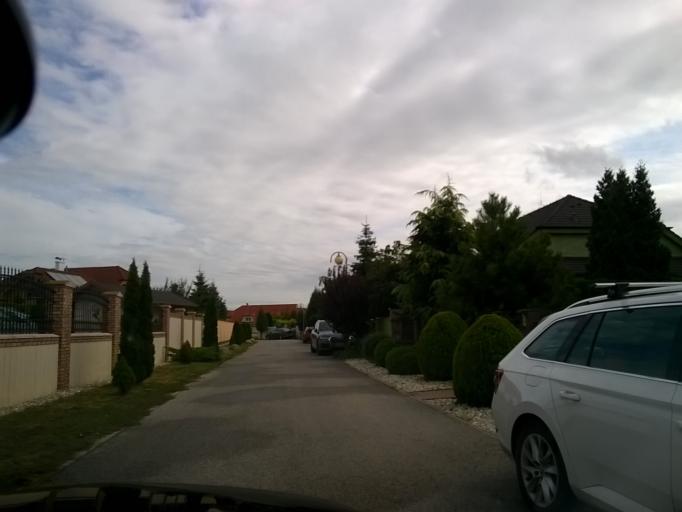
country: SK
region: Nitriansky
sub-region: Okres Nitra
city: Nitra
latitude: 48.2954
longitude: 18.0533
